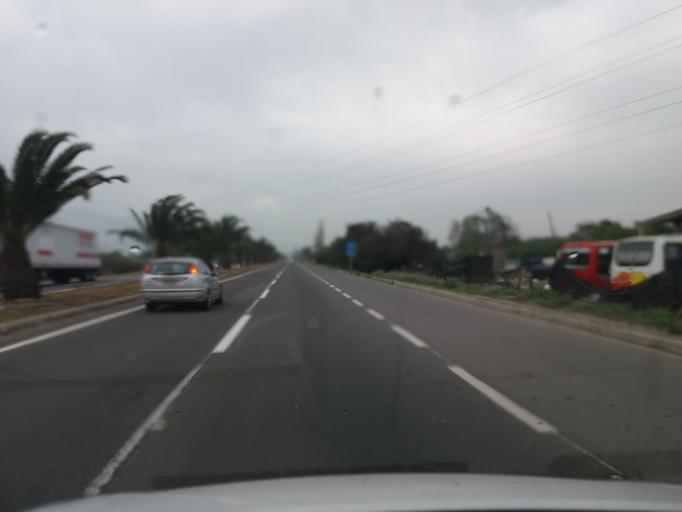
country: CL
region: Valparaiso
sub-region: Provincia de Quillota
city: Hacienda La Calera
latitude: -32.7748
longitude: -71.1847
